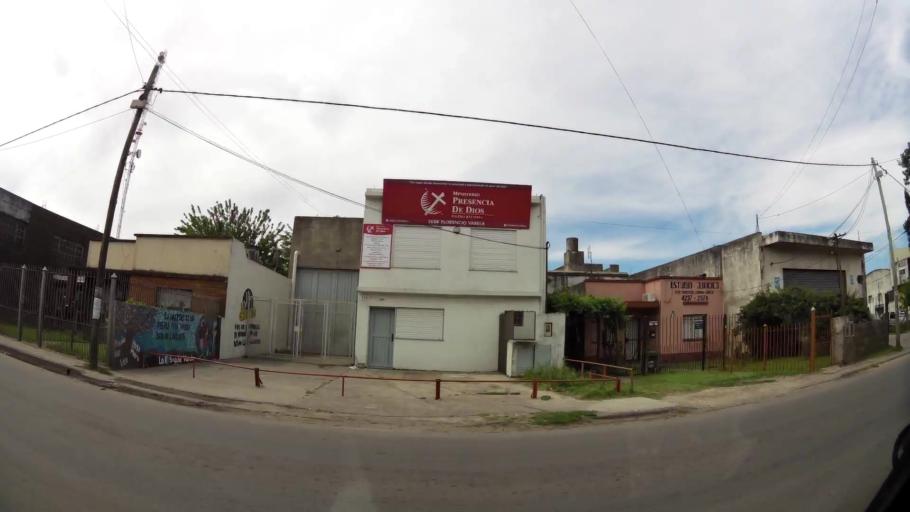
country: AR
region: Buenos Aires
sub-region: Partido de Quilmes
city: Quilmes
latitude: -34.7788
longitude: -58.2664
